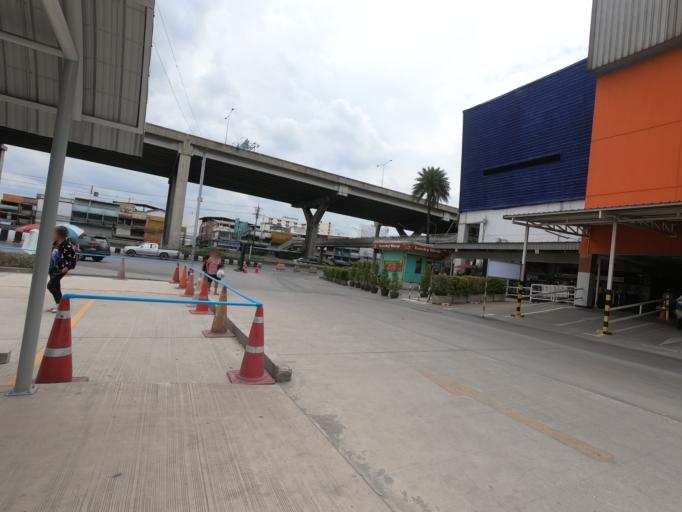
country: TH
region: Bangkok
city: Sai Mai
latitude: 13.9181
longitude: 100.6549
